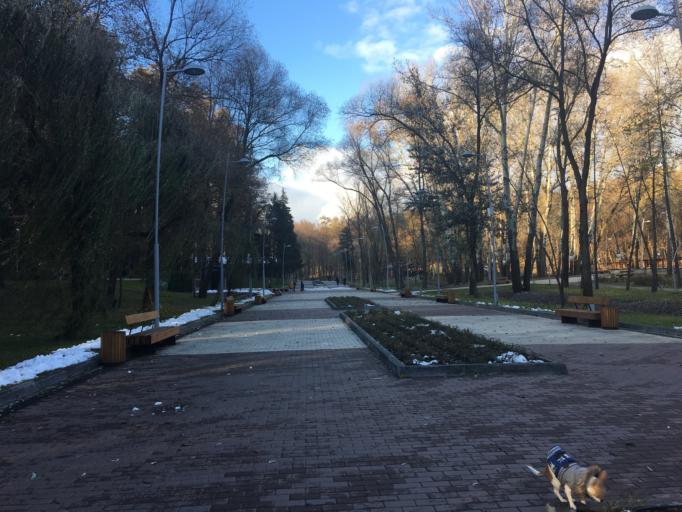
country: RU
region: Voronezj
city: Voronezh
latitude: 51.6980
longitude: 39.2184
